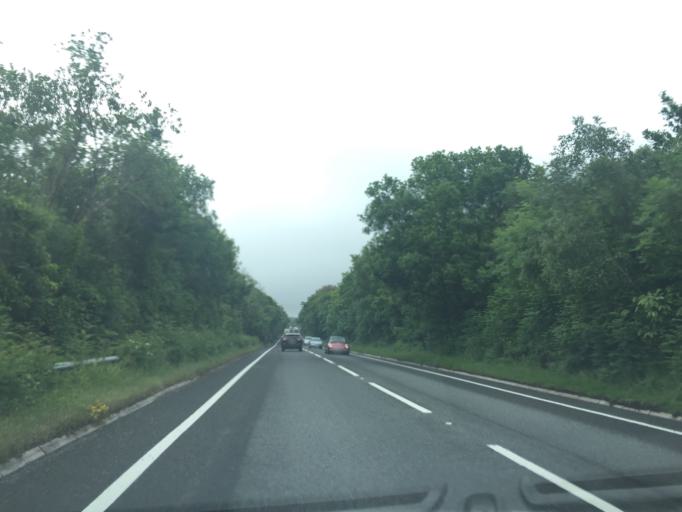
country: GB
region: England
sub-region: Dorset
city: Wareham
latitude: 50.6486
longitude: -2.0746
